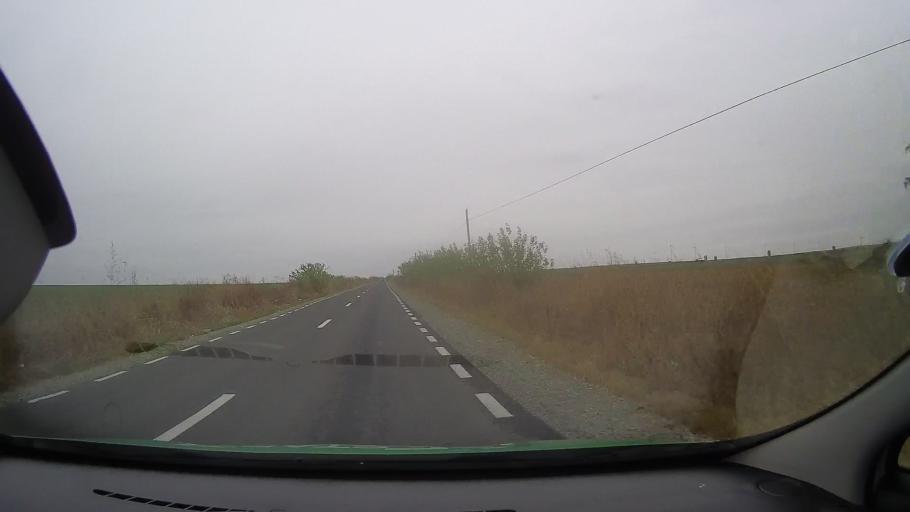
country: RO
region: Constanta
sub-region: Comuna Tortoman
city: Tortoman
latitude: 44.3681
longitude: 28.2077
